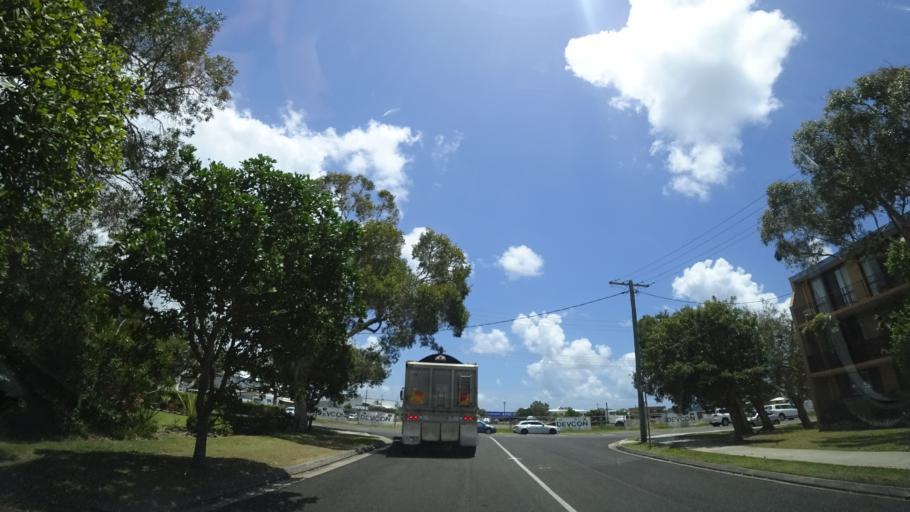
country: AU
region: Queensland
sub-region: Sunshine Coast
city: Coolum Beach
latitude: -26.5292
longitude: 153.0888
